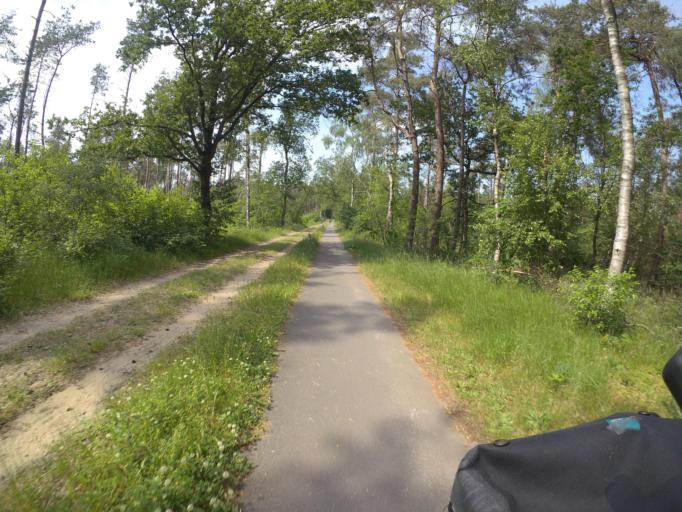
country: NL
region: Overijssel
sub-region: Gemeente Twenterand
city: Den Ham
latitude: 52.3842
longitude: 6.4382
